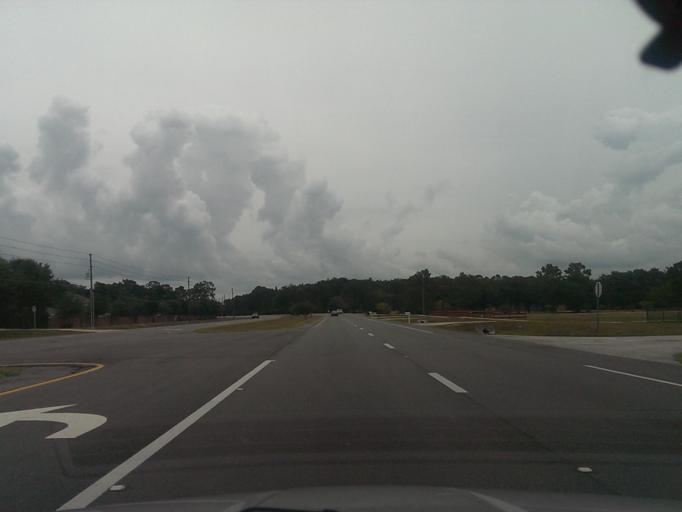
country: US
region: Florida
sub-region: Orange County
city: Bay Hill
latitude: 28.4309
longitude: -81.5328
